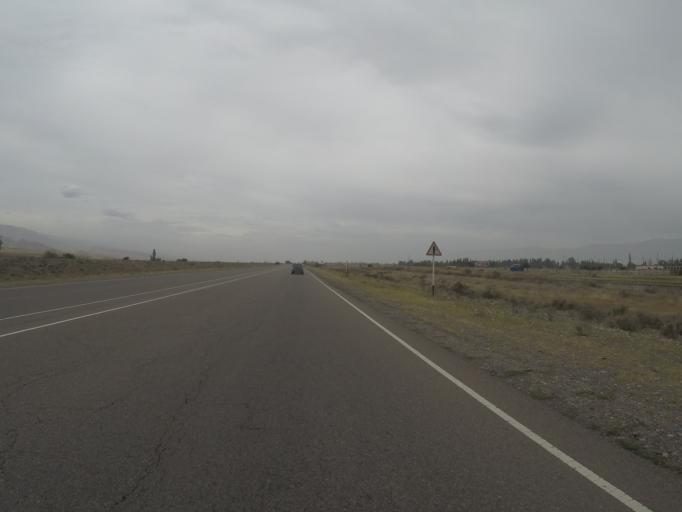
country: KG
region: Chuy
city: Bystrovka
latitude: 42.8296
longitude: 75.5225
